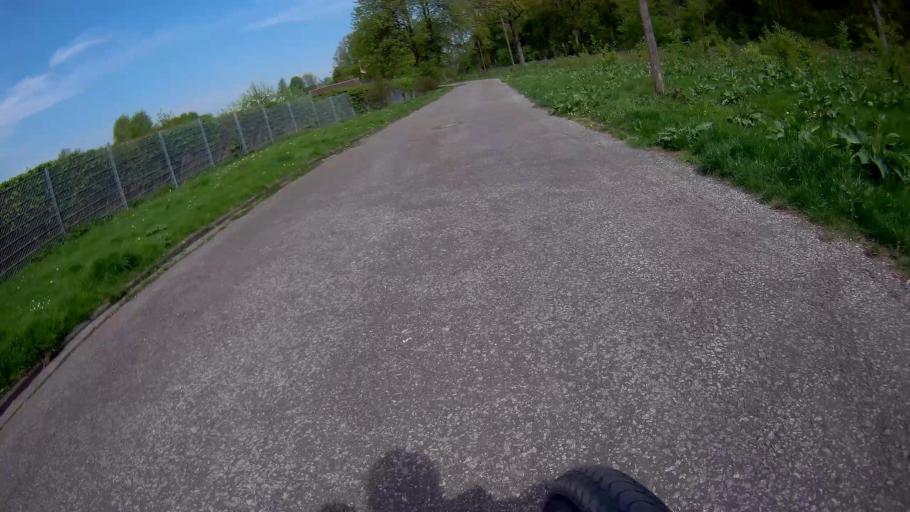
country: DE
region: North Rhine-Westphalia
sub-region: Regierungsbezirk Munster
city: Gelsenkirchen
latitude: 51.5574
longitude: 7.1017
